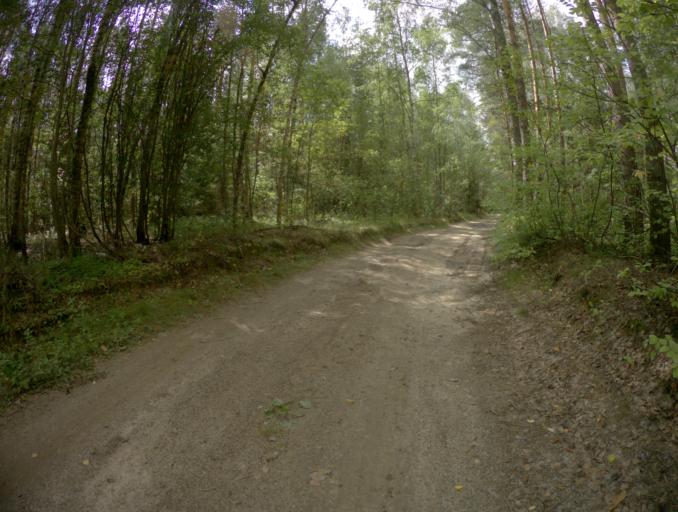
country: RU
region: Vladimir
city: Raduzhnyy
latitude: 55.9667
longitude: 40.2179
